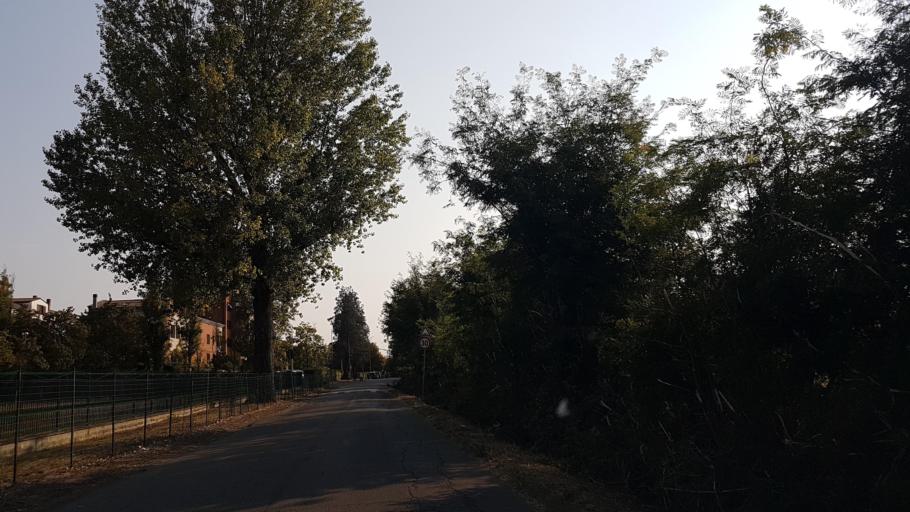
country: IT
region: Emilia-Romagna
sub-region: Provincia di Parma
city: Vicofertile
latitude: 44.7838
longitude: 10.2838
